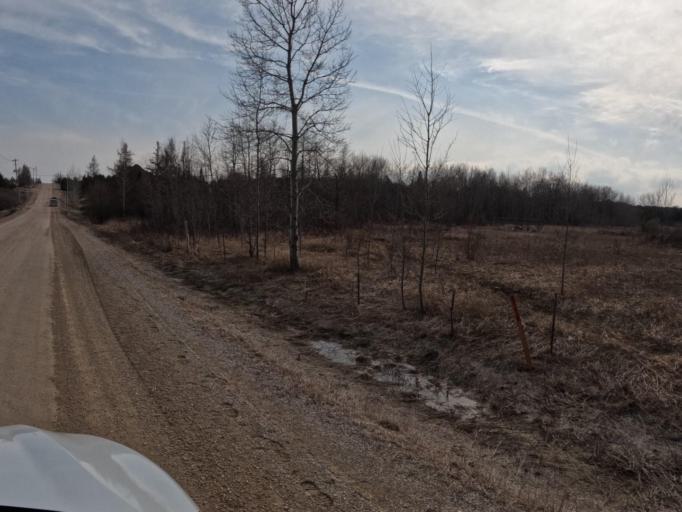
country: CA
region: Ontario
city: Orangeville
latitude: 43.8912
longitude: -80.2993
